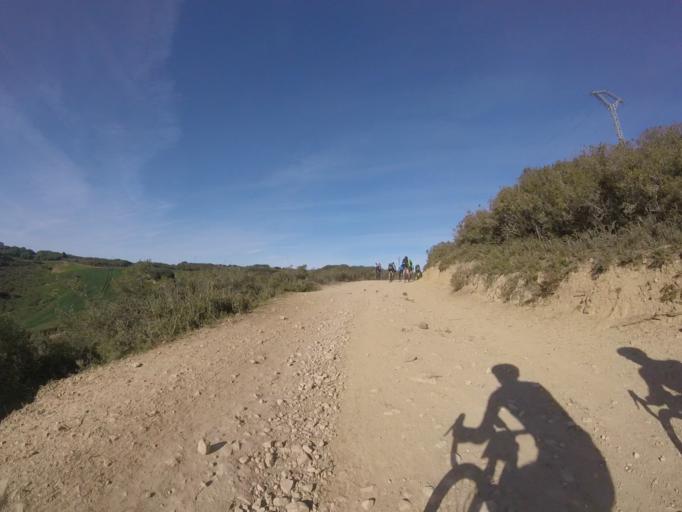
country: ES
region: Navarre
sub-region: Provincia de Navarra
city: Yerri
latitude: 42.6988
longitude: -1.9641
